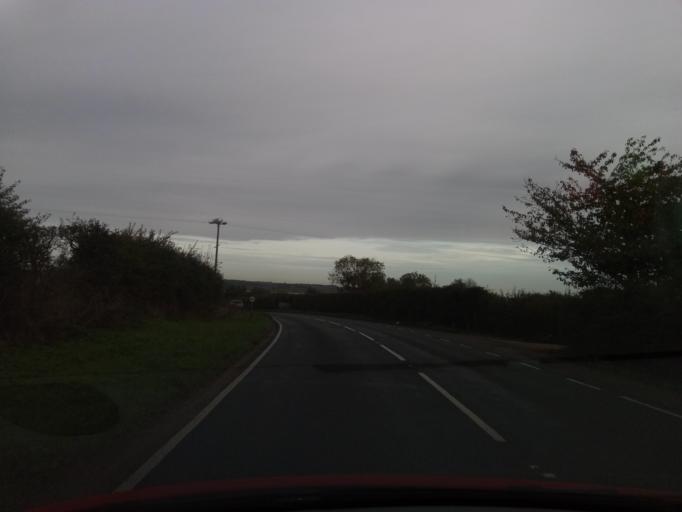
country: GB
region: England
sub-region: Essex
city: West Mersea
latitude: 51.7883
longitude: 0.9212
